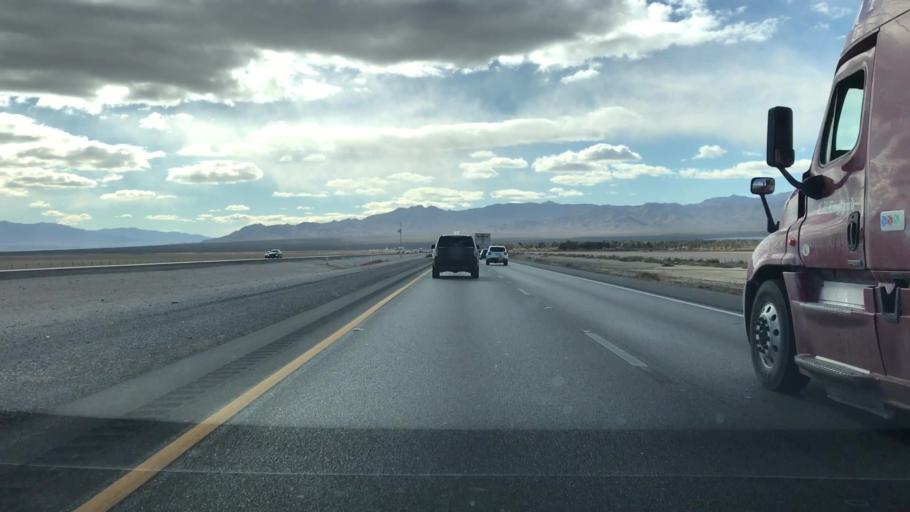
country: US
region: Nevada
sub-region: Clark County
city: Sandy Valley
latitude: 35.5696
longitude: -115.4076
